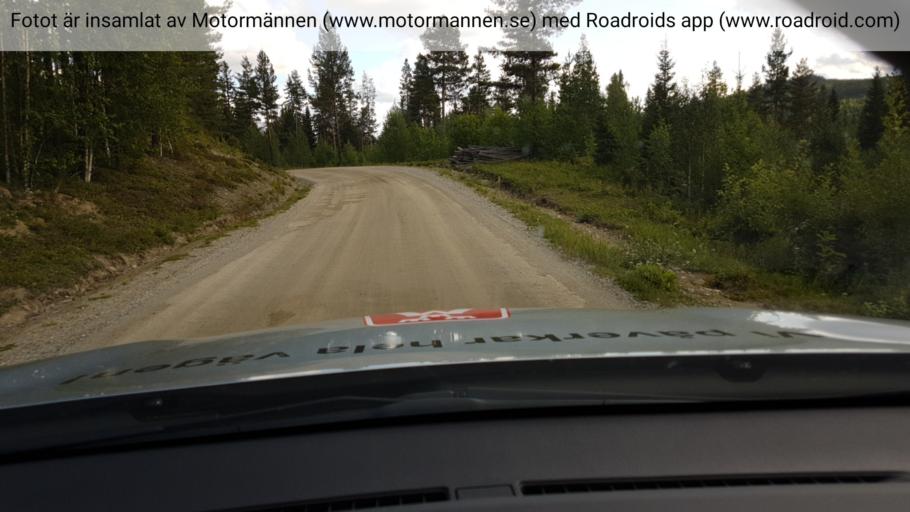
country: SE
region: Jaemtland
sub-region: Ragunda Kommun
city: Hammarstrand
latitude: 63.3468
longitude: 15.9774
